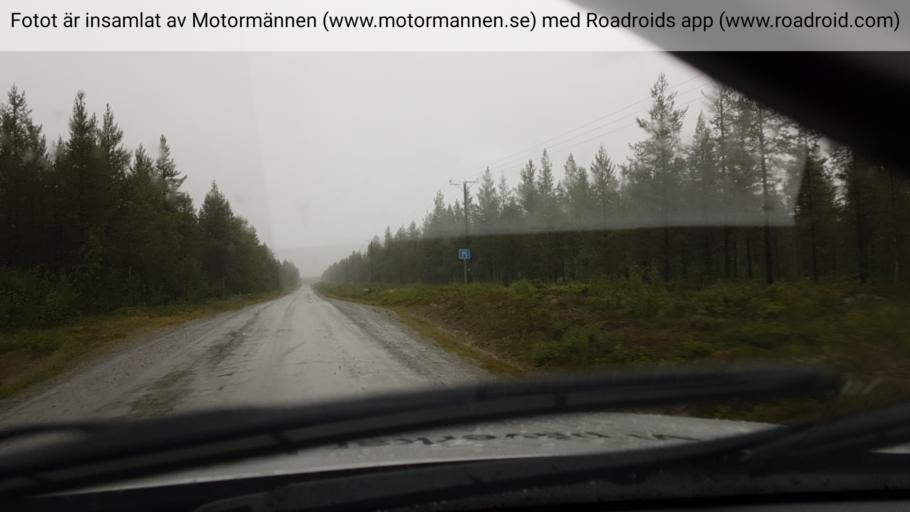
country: SE
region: Norrbotten
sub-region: Jokkmokks Kommun
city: Jokkmokk
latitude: 66.6110
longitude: 18.9642
